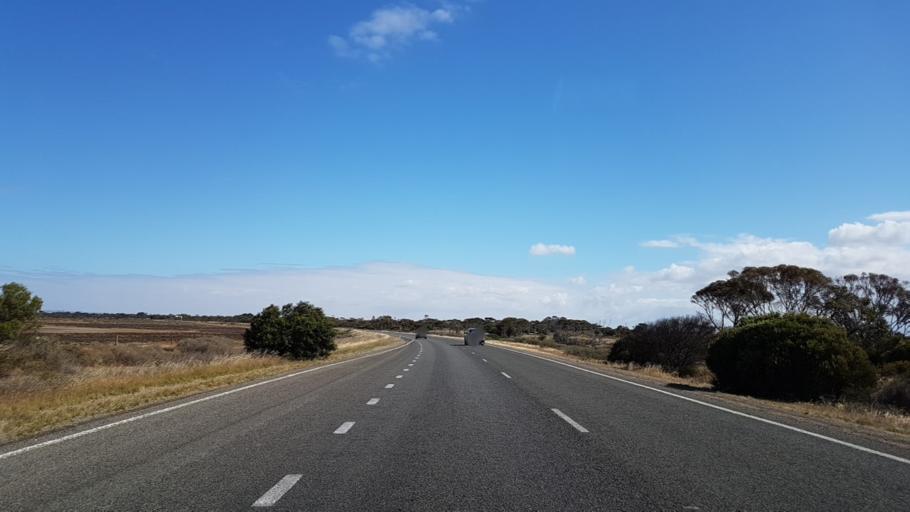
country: AU
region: South Australia
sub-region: Wakefield
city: Balaklava
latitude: -34.2871
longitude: 138.2417
